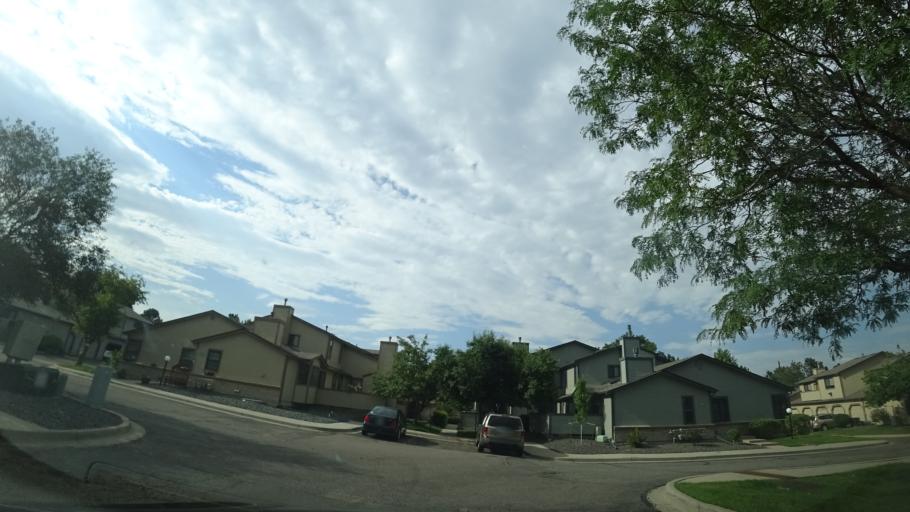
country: US
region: Colorado
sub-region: Jefferson County
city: Lakewood
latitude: 39.7141
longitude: -105.0978
